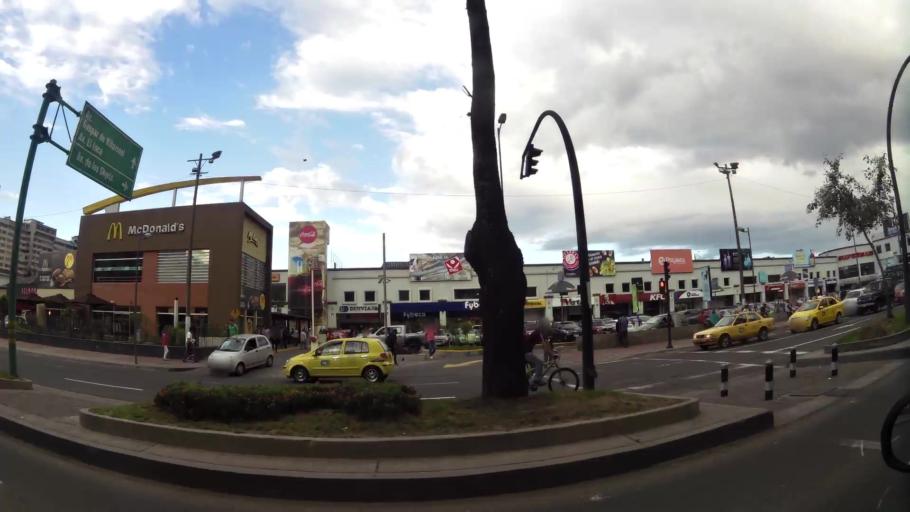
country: EC
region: Pichincha
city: Quito
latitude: -0.1769
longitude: -78.4858
